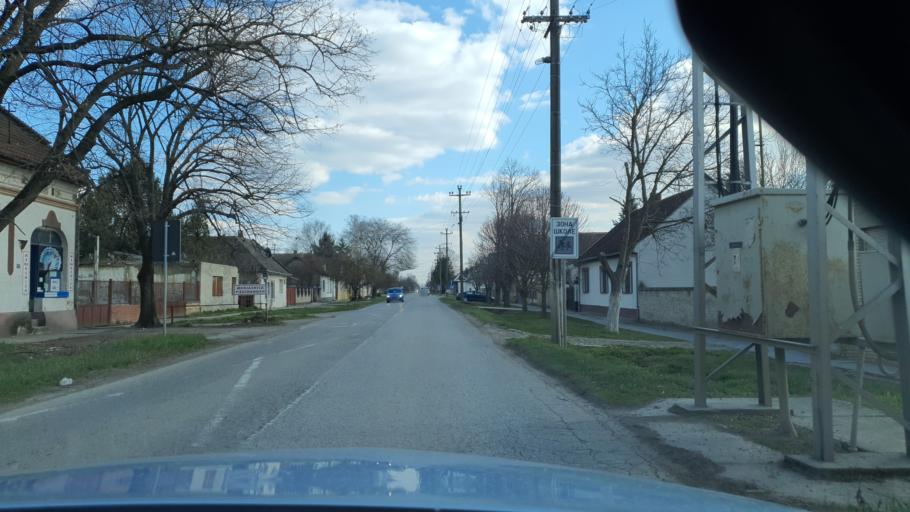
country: RS
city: Ravno Selo
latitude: 45.4494
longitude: 19.6203
